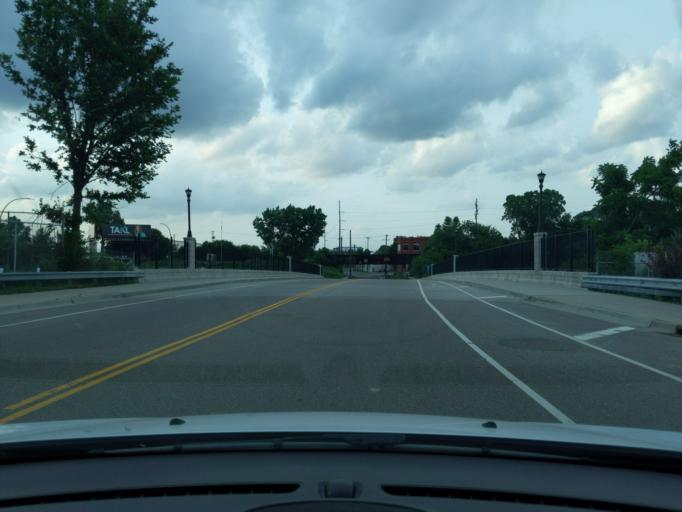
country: US
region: Minnesota
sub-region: Ramsey County
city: Falcon Heights
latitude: 44.9523
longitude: -93.1827
